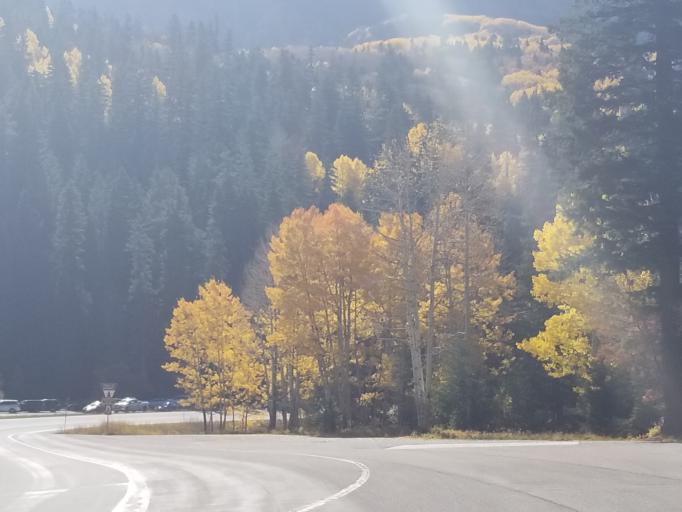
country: US
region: Colorado
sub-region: Archuleta County
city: Pagosa Springs
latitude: 37.4442
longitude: -106.8786
